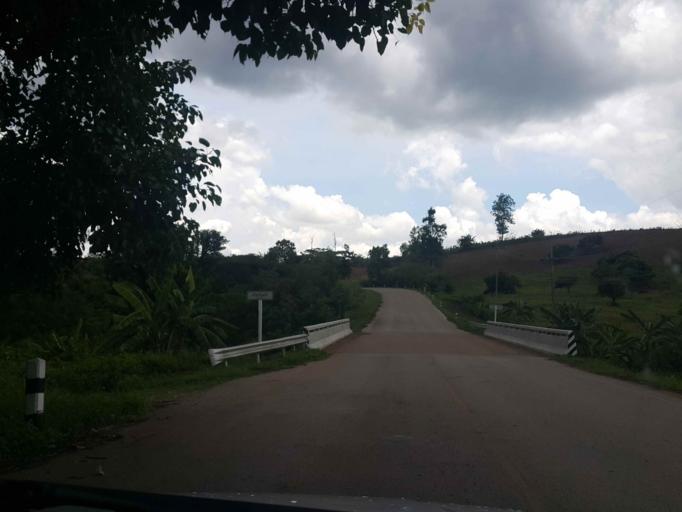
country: TH
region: Phayao
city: Dok Kham Tai
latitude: 18.9676
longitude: 100.0745
